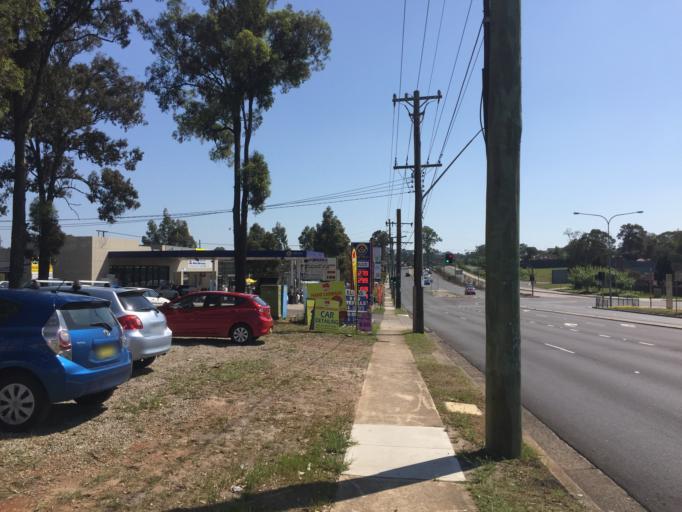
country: AU
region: New South Wales
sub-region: Blacktown
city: Blacktown
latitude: -33.7536
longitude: 150.9150
